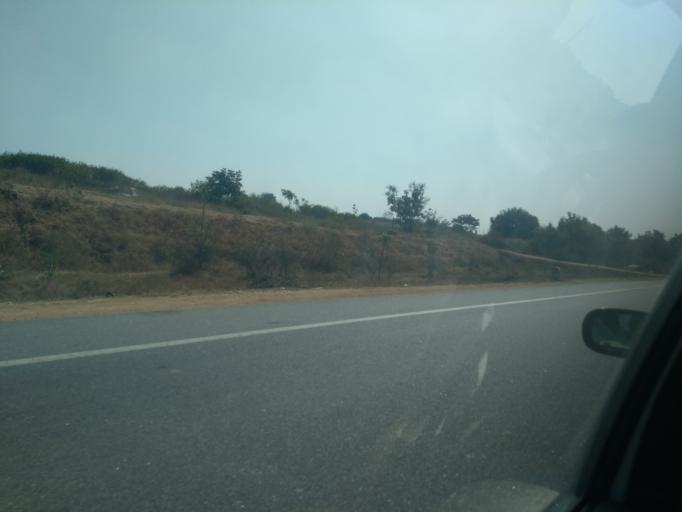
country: IN
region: Telangana
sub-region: Mahbubnagar
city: Mahbubnagar
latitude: 16.7422
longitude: 78.1000
